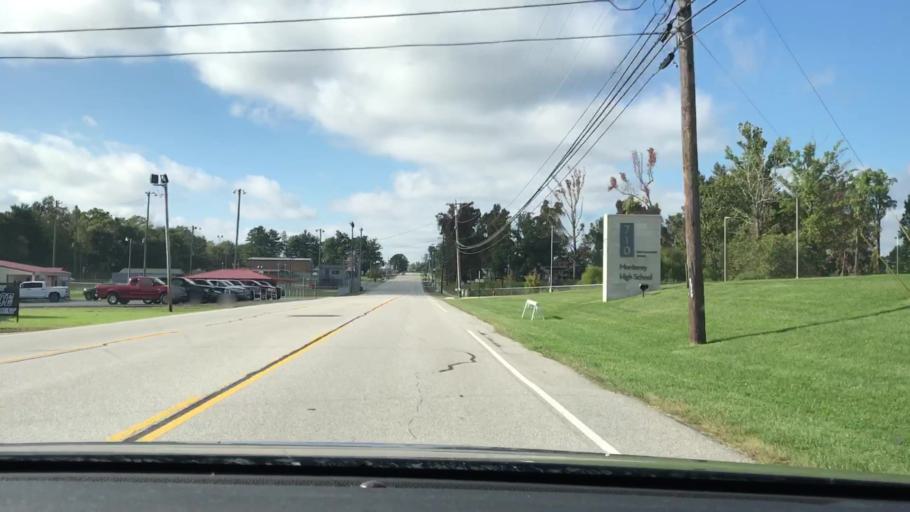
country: US
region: Tennessee
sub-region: Putnam County
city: Monterey
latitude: 36.1415
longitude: -85.2609
